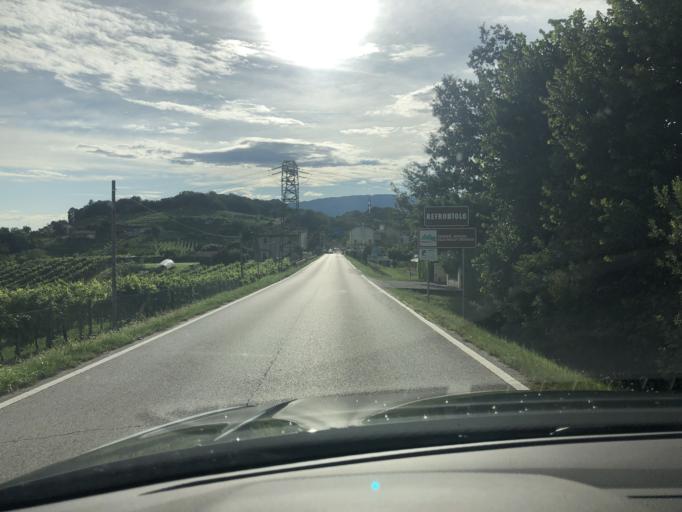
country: IT
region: Veneto
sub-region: Provincia di Treviso
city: Corbanese
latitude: 45.9333
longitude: 12.2319
